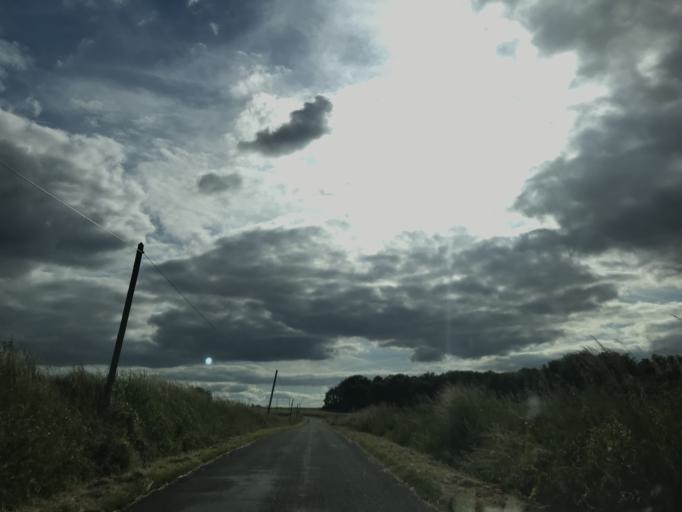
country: FR
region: Aquitaine
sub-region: Departement de la Dordogne
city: Saint-Aulaye
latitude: 45.2500
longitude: 0.1240
